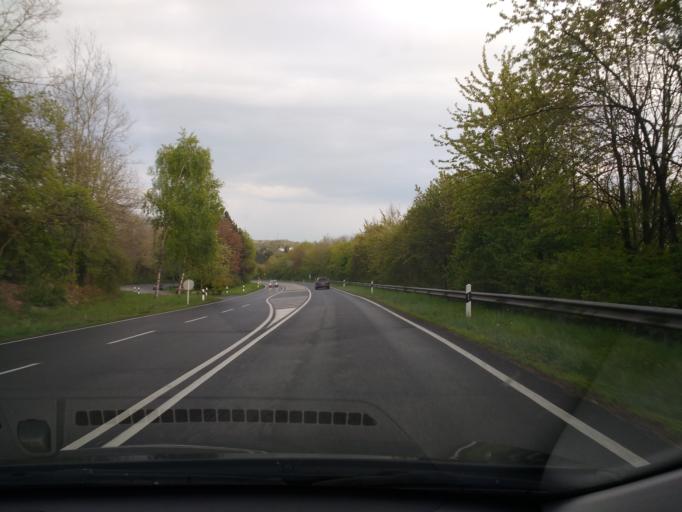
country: LU
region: Luxembourg
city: Moutfort
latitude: 49.5777
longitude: 6.2685
